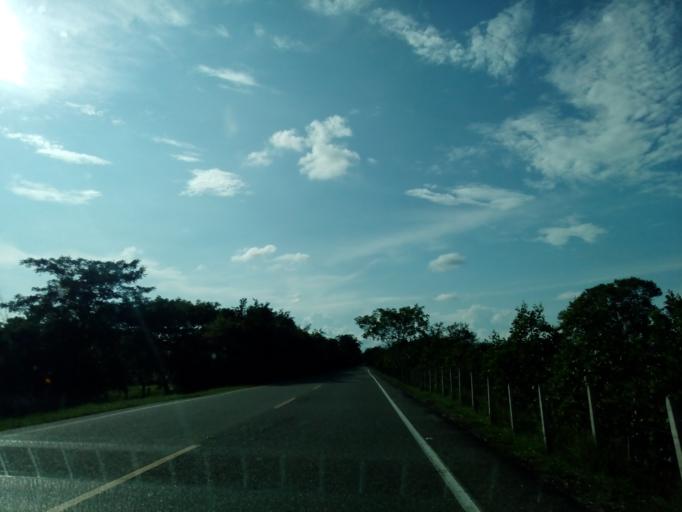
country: CO
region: Boyaca
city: Puerto Boyaca
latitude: 5.9373
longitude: -74.5517
